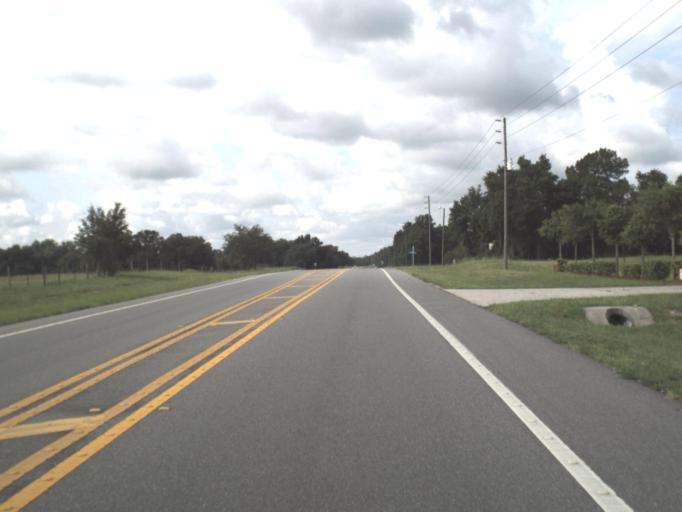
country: US
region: Florida
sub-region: Hernando County
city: Ridge Manor
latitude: 28.5001
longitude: -82.1723
